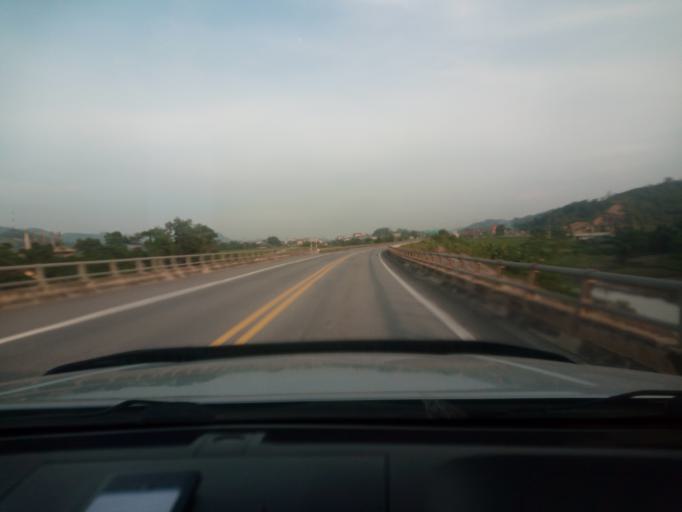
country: VN
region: Yen Bai
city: Co Phuc
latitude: 21.8840
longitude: 104.6679
